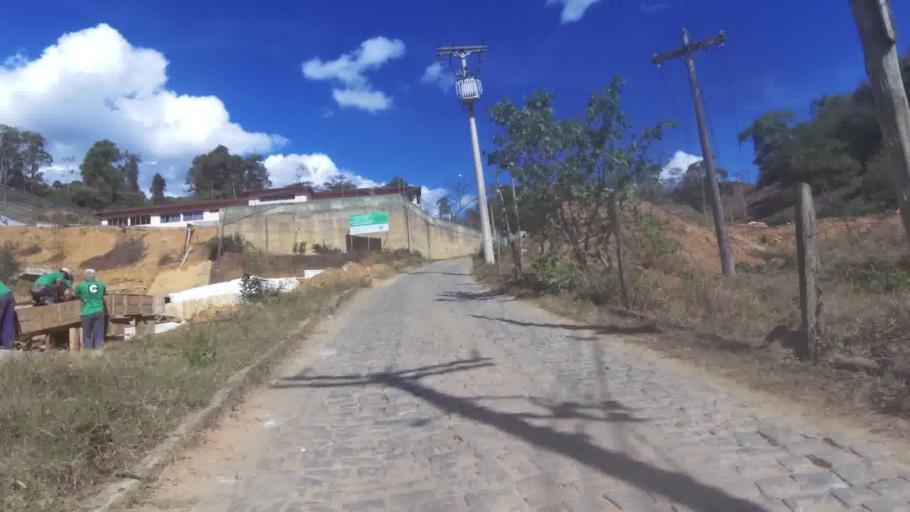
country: BR
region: Espirito Santo
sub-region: Vargem Alta
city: Vargem Alta
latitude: -20.6635
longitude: -41.0562
